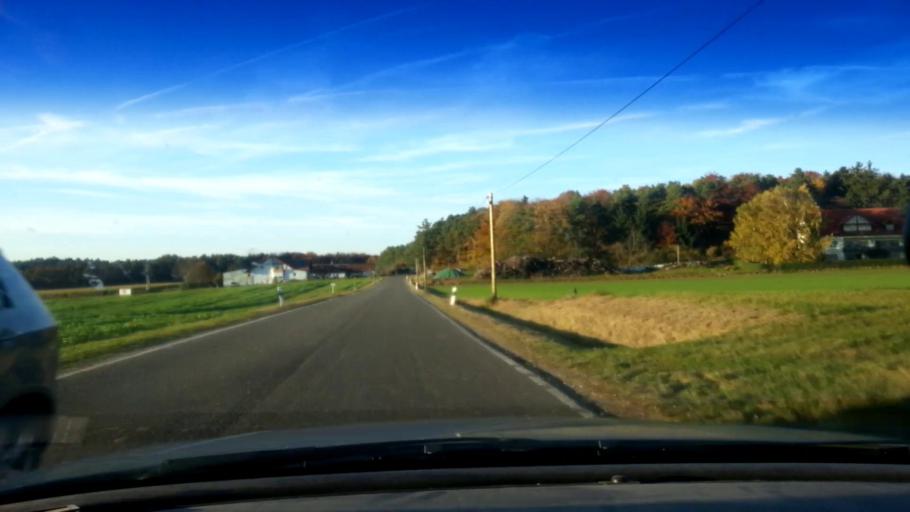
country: DE
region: Bavaria
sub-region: Upper Franconia
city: Unterleinleiter
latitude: 49.8557
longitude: 11.2112
